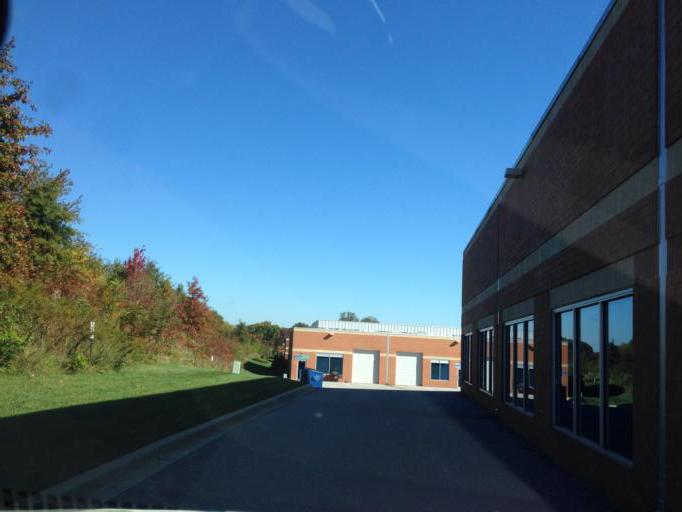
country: US
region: Maryland
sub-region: Howard County
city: Fulton
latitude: 39.1511
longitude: -76.9113
